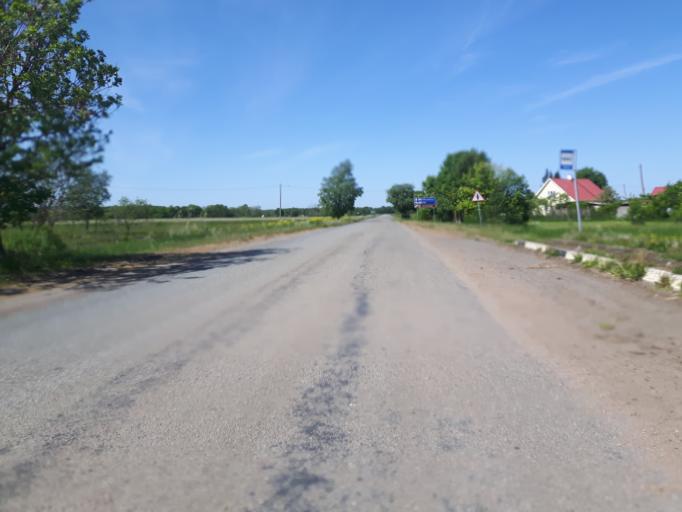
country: EE
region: Ida-Virumaa
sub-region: Aseri vald
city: Aseri
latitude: 59.4749
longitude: 26.7951
